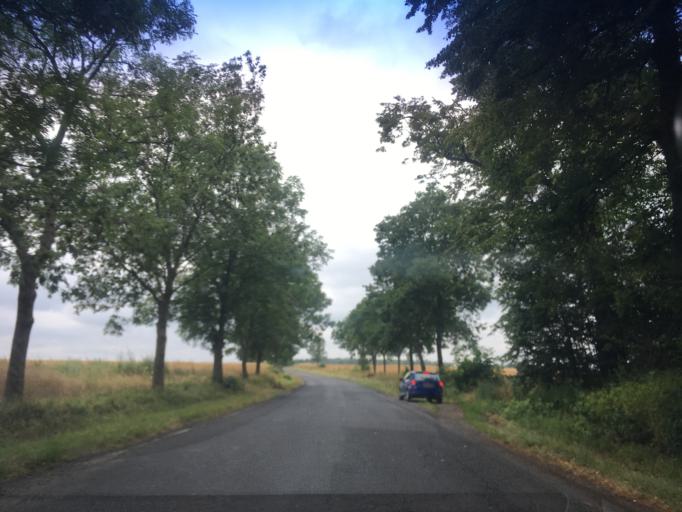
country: PL
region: Lower Silesian Voivodeship
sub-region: Powiat zgorzelecki
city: Sulikow
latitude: 51.0762
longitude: 15.0442
